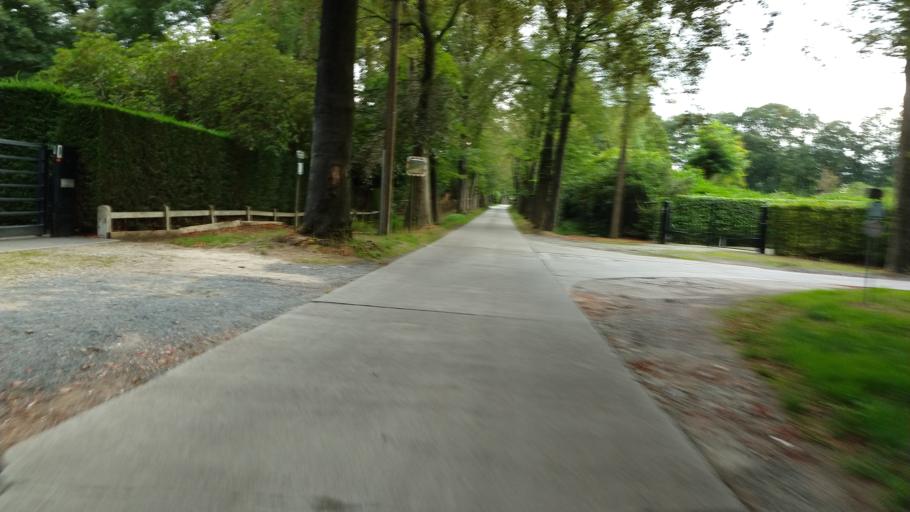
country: BE
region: Flanders
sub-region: Provincie Oost-Vlaanderen
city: Aalter
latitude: 51.0756
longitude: 3.4602
